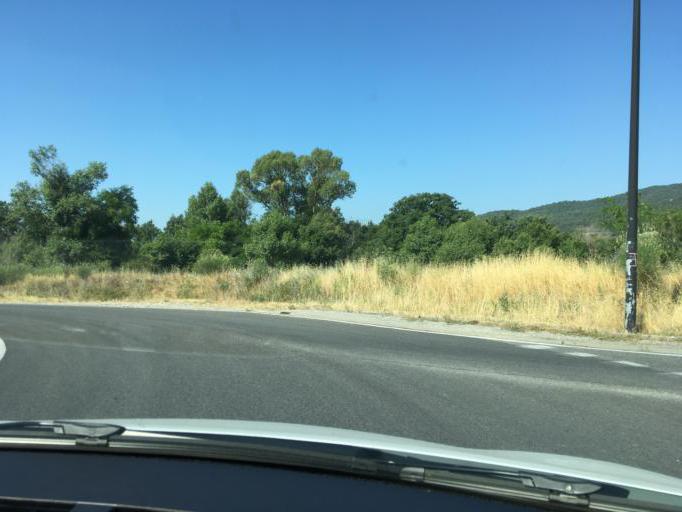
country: FR
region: Provence-Alpes-Cote d'Azur
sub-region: Departement des Alpes-de-Haute-Provence
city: Peyruis
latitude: 44.0406
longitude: 5.9588
